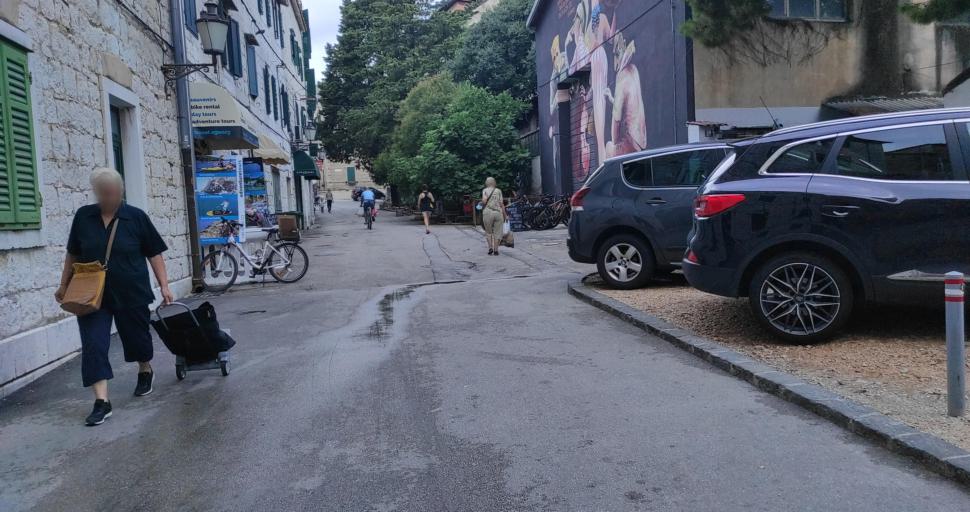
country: HR
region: Splitsko-Dalmatinska
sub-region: Grad Split
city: Split
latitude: 43.5111
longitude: 16.4352
